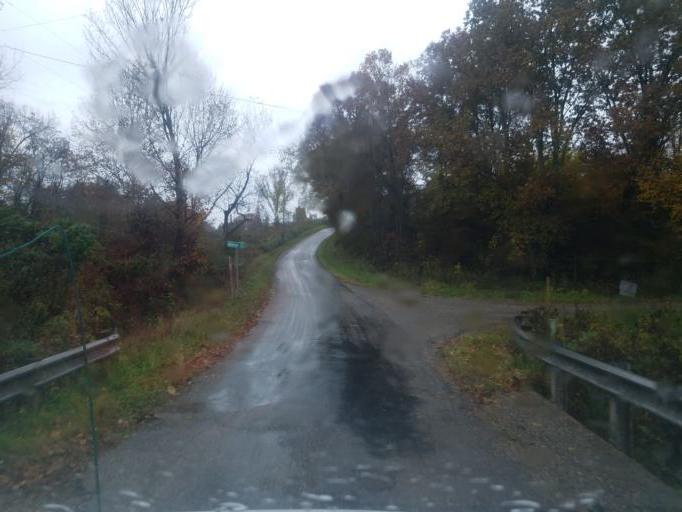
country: US
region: Ohio
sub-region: Washington County
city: Belpre
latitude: 39.3173
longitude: -81.6036
